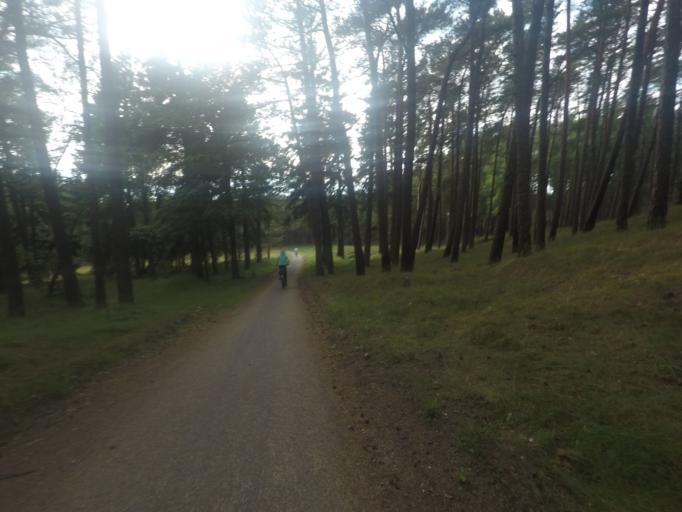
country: LT
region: Klaipedos apskritis
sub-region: Klaipeda
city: Klaipeda
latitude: 55.6434
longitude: 21.1172
